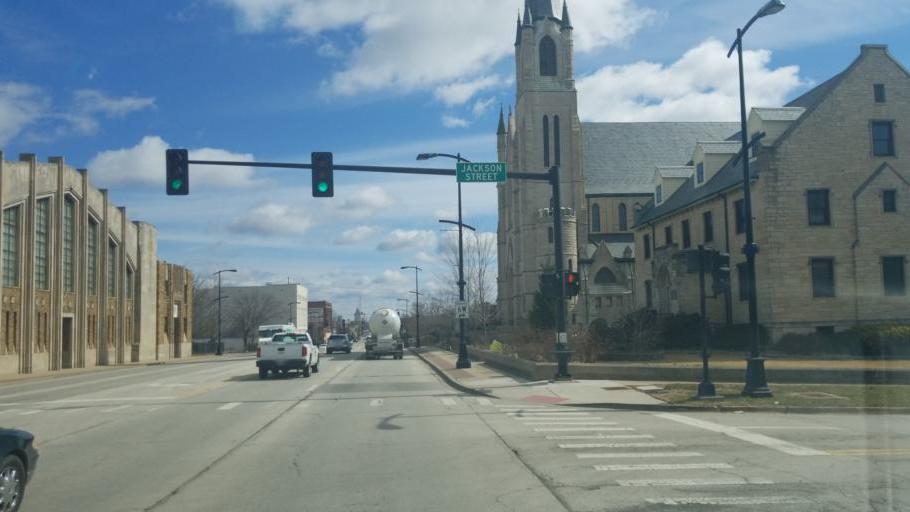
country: US
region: Illinois
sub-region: Macon County
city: Decatur
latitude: 39.8458
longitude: -88.9518
